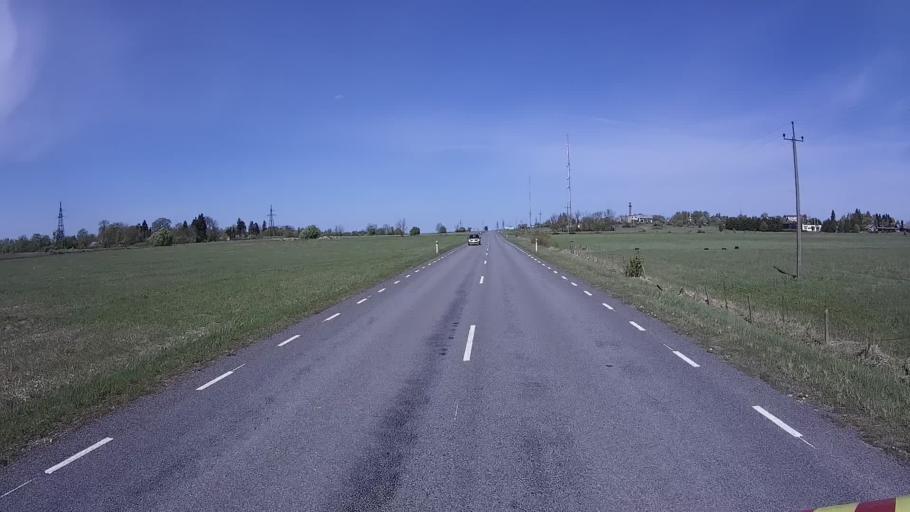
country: EE
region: Laeaene
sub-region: Lihula vald
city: Lihula
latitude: 58.6700
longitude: 23.8287
